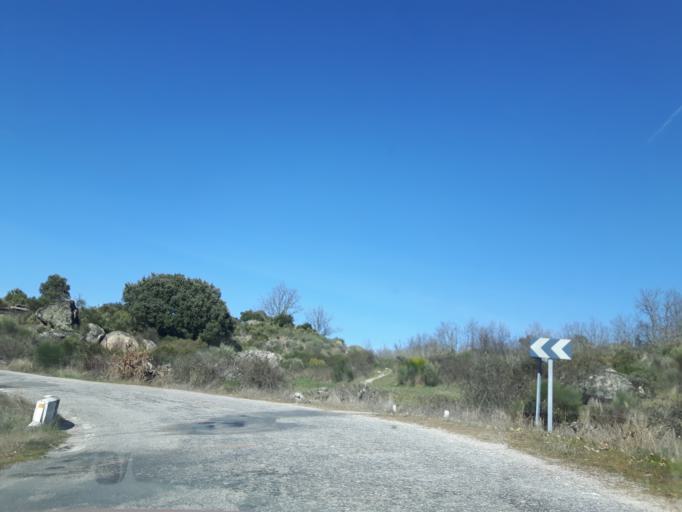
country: ES
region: Castille and Leon
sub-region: Provincia de Salamanca
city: Saldeana
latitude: 41.0019
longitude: -6.6265
